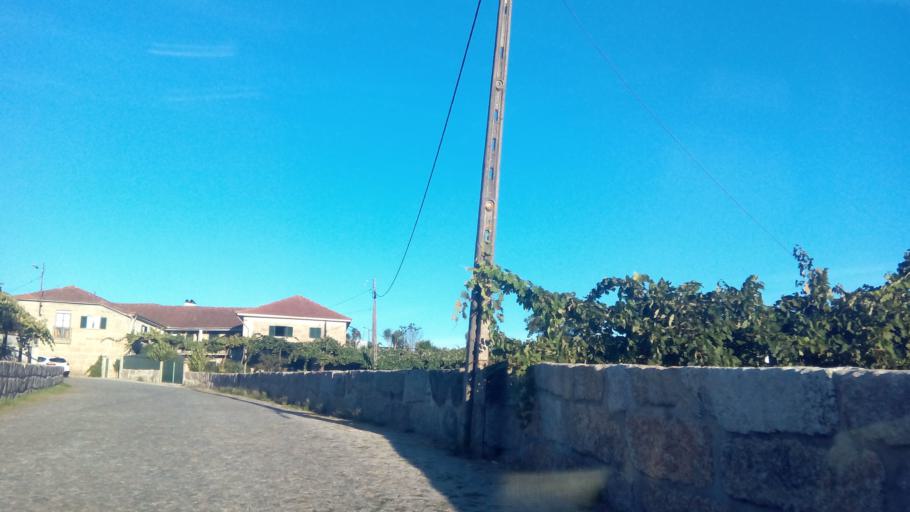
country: PT
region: Porto
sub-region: Paredes
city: Baltar
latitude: 41.1838
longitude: -8.3796
